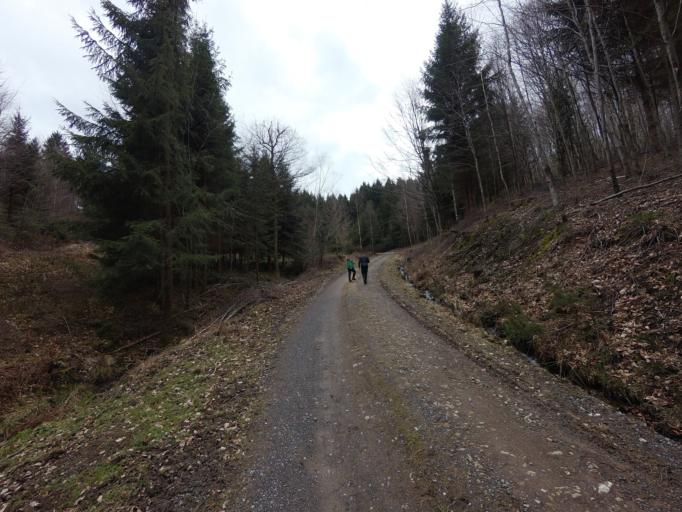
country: BE
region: Wallonia
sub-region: Province de Liege
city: Aywaille
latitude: 50.4288
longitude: 5.7240
